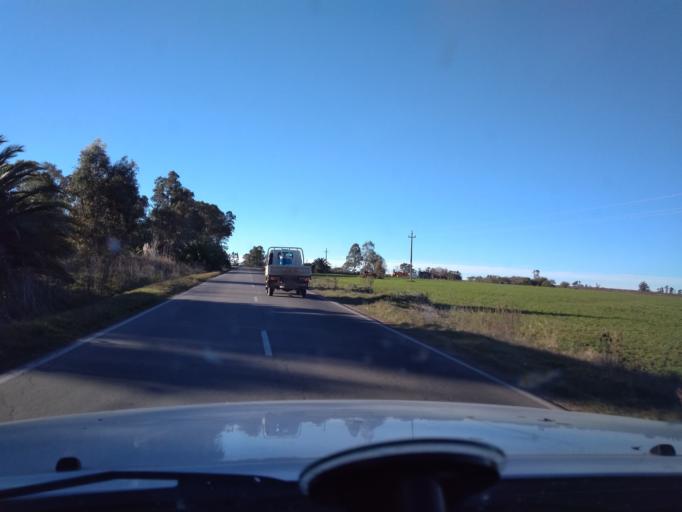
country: UY
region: Canelones
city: San Bautista
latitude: -34.4664
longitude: -56.0058
